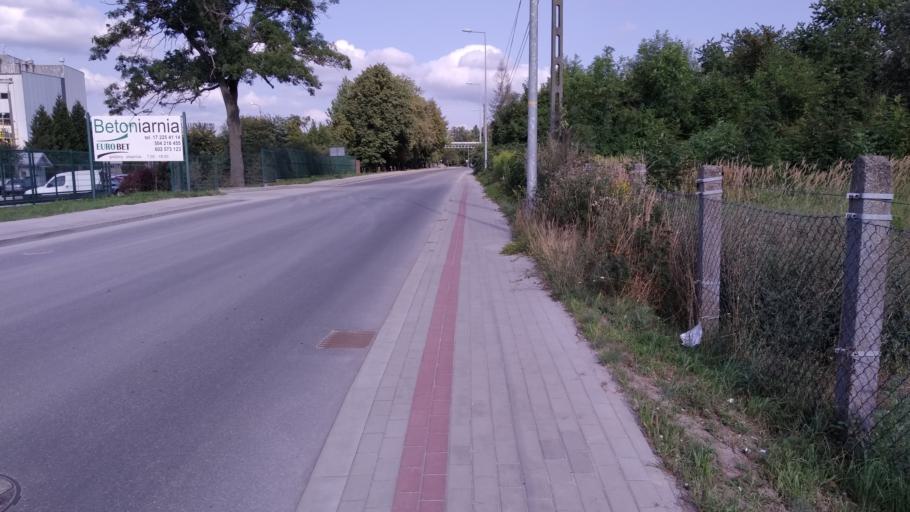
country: PL
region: Subcarpathian Voivodeship
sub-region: Powiat lancucki
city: Lancut
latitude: 50.0787
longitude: 22.2241
